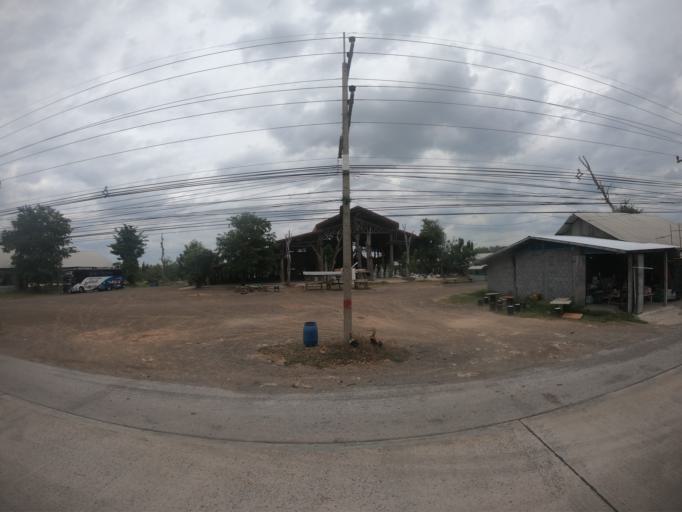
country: TH
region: Nakhon Ratchasima
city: Chok Chai
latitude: 14.8004
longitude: 102.1714
